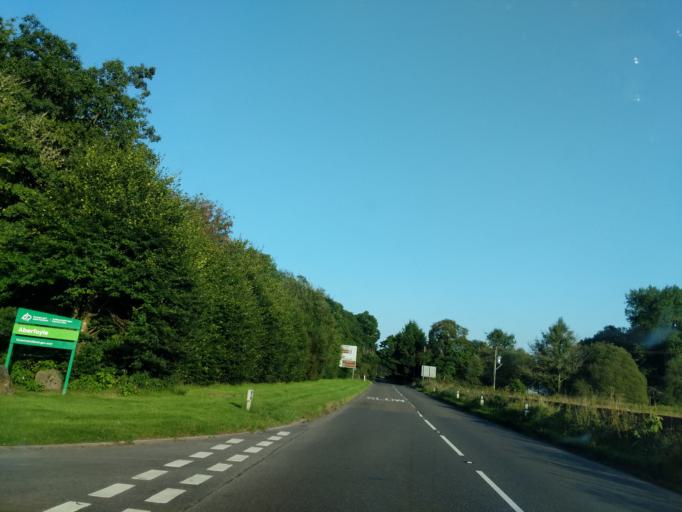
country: GB
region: Scotland
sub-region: Stirling
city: Balfron
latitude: 56.1731
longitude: -4.3692
